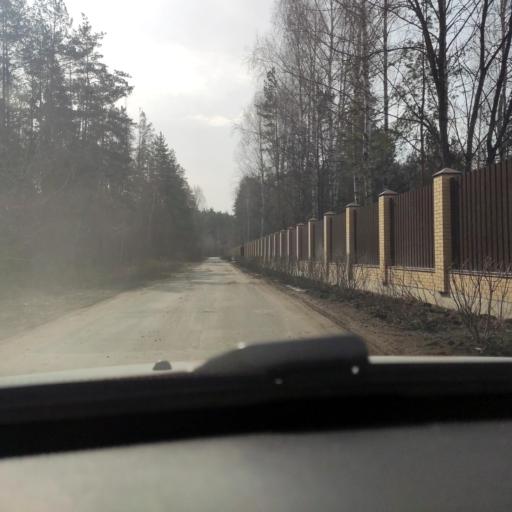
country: RU
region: Voronezj
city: Ramon'
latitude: 51.8994
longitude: 39.3669
